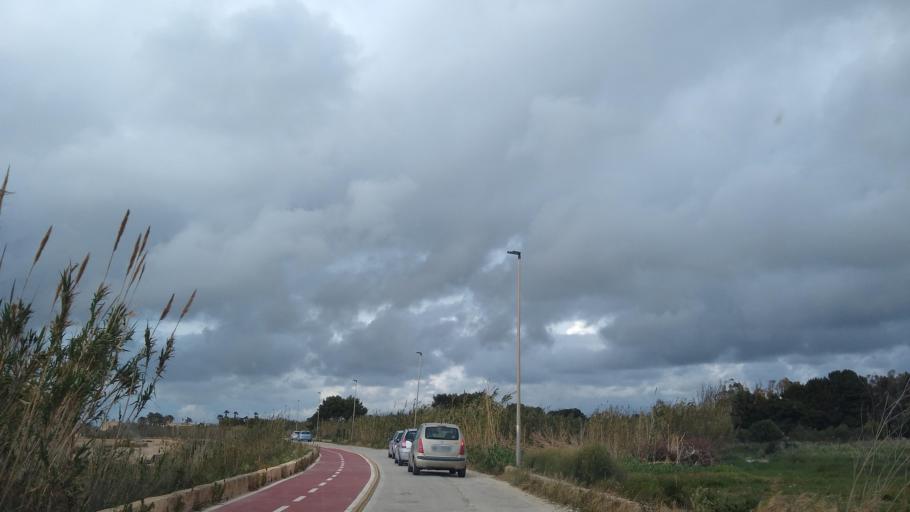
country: IT
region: Sicily
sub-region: Trapani
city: Marsala
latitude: 37.8579
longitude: 12.4845
